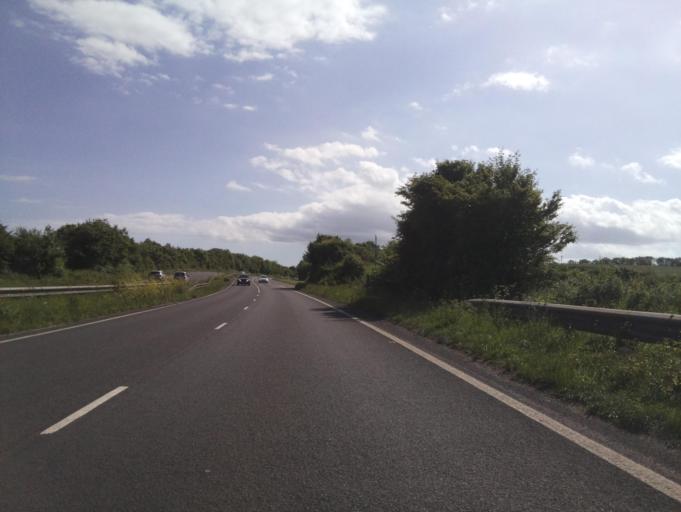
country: GB
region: England
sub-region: Devon
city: Marldon
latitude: 50.4665
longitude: -3.5842
